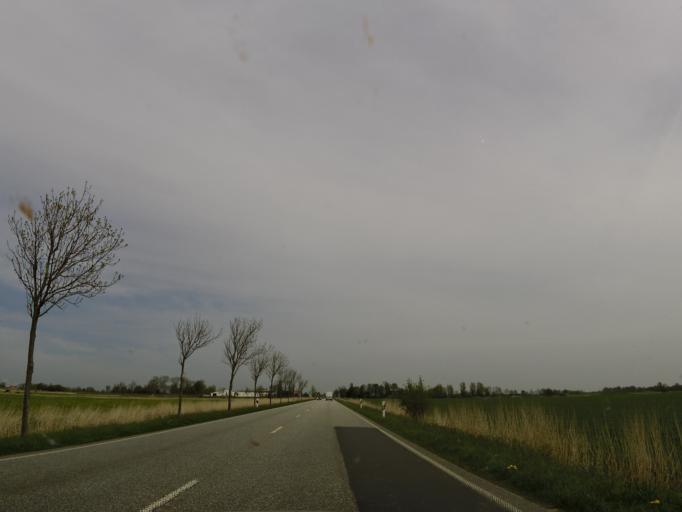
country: DE
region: Schleswig-Holstein
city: Koldenbuttel
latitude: 54.4088
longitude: 9.0384
